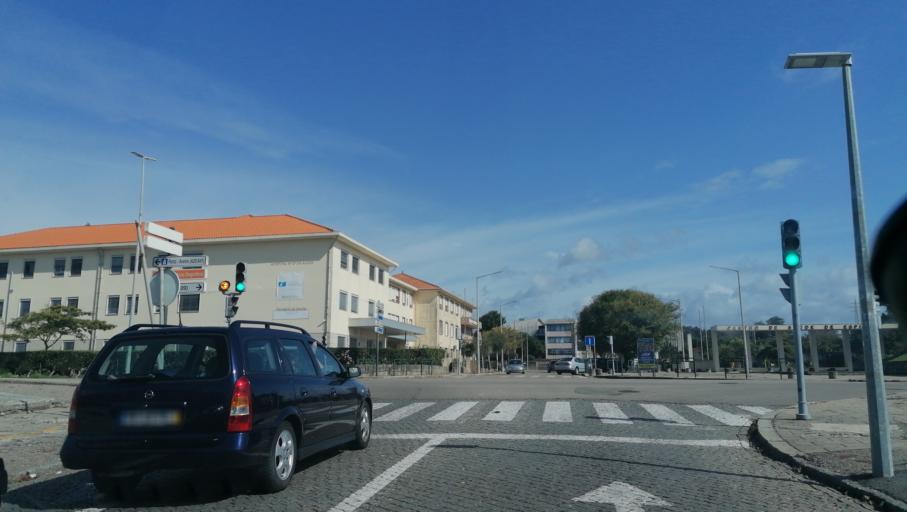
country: PT
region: Aveiro
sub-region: Espinho
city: Espinho
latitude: 41.0023
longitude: -8.6385
